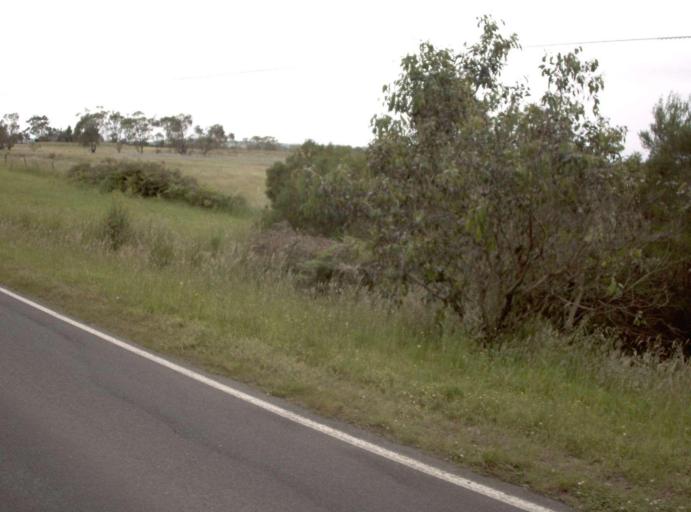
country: AU
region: Victoria
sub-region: Baw Baw
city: Warragul
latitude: -38.5768
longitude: 146.0316
